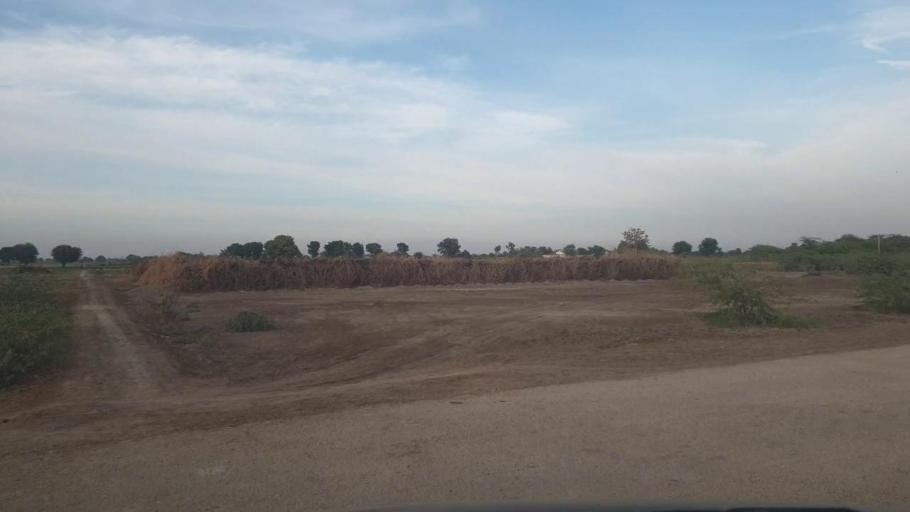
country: PK
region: Sindh
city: Kunri
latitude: 25.2385
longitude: 69.5562
